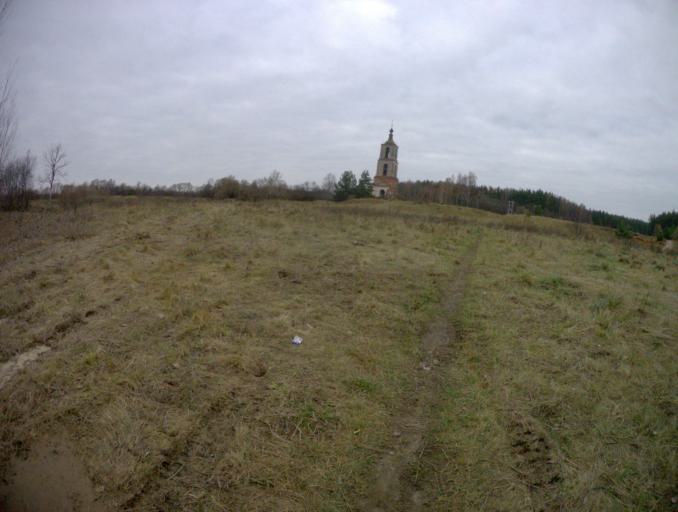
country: RU
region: Moskovskaya
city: Malaya Dubna
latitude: 55.9917
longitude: 38.9960
